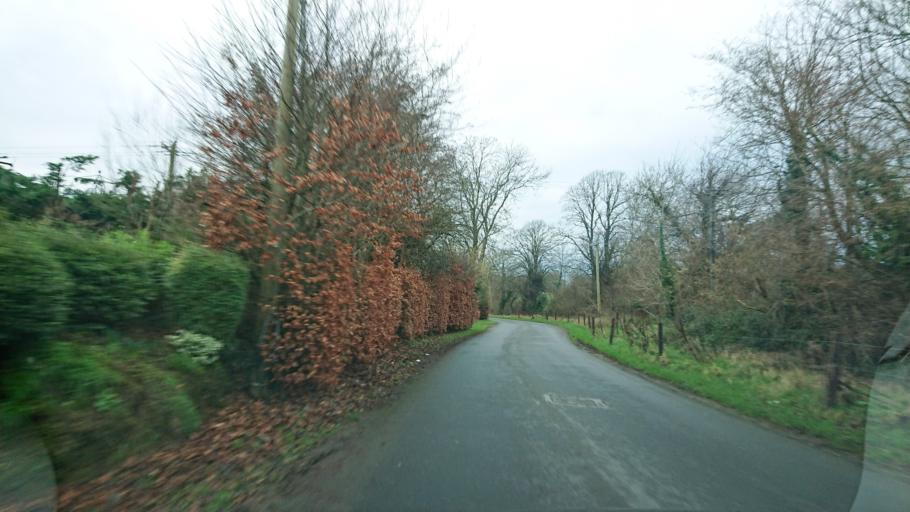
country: IE
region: Leinster
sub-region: Kilkenny
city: Mooncoin
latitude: 52.2316
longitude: -7.2459
